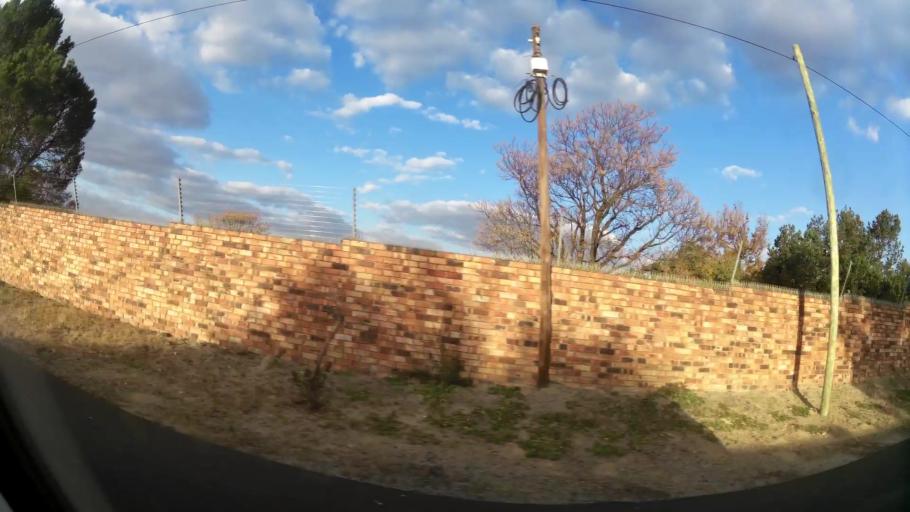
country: ZA
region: Gauteng
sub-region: City of Johannesburg Metropolitan Municipality
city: Diepsloot
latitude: -25.9948
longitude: 27.9689
